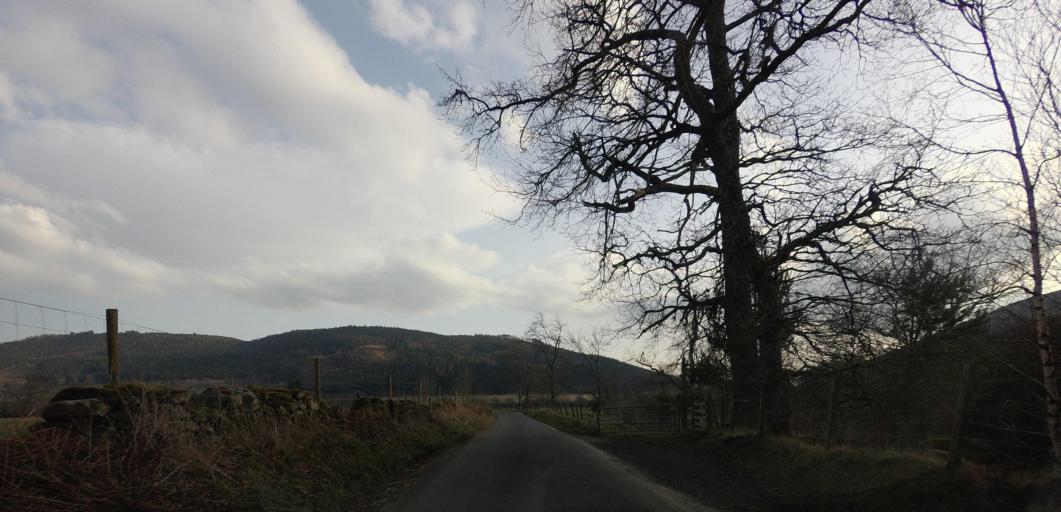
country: GB
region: Scotland
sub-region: Perth and Kinross
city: Aberfeldy
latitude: 56.5998
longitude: -4.0715
